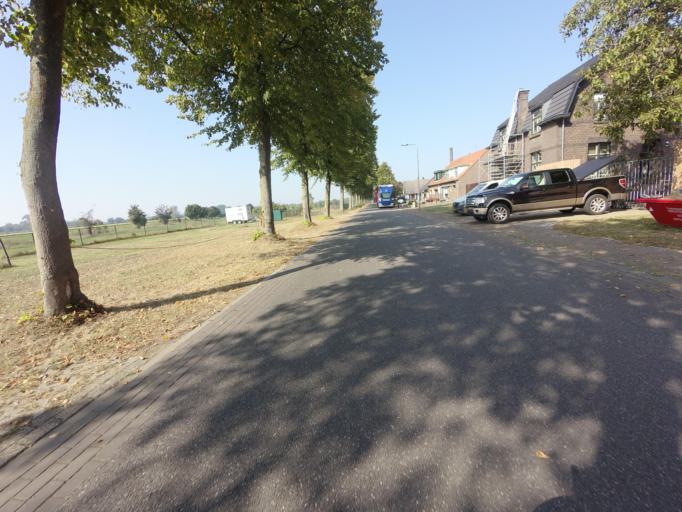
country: NL
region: Limburg
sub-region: Gemeente Roermond
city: Leeuwen
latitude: 51.2290
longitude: 5.9864
